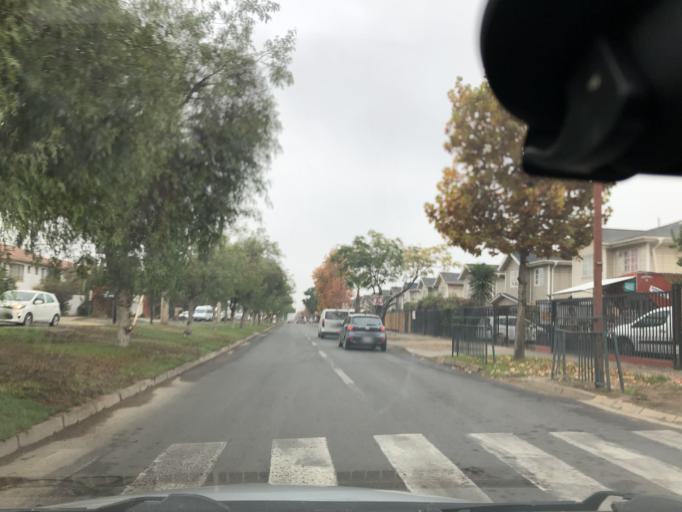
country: CL
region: Santiago Metropolitan
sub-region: Provincia de Cordillera
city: Puente Alto
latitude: -33.5986
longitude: -70.5819
